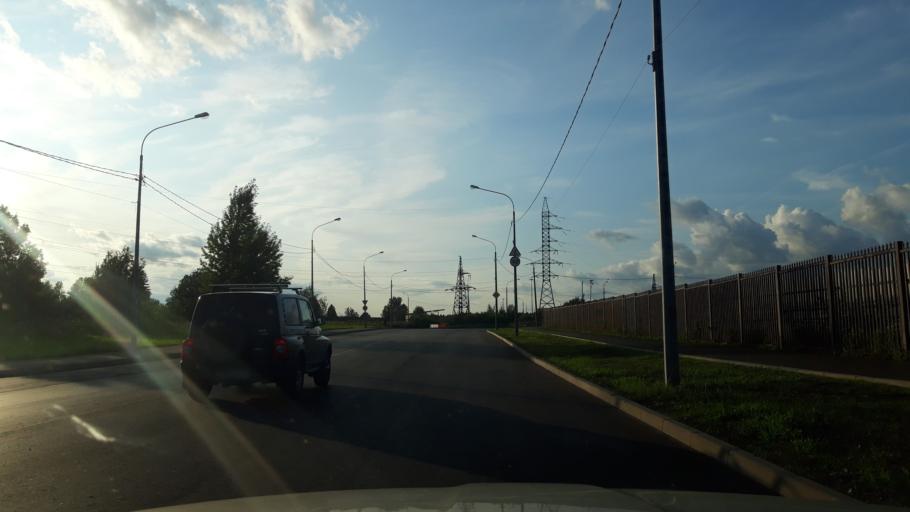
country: RU
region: Moskovskaya
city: Alabushevo
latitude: 56.0106
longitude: 37.1406
